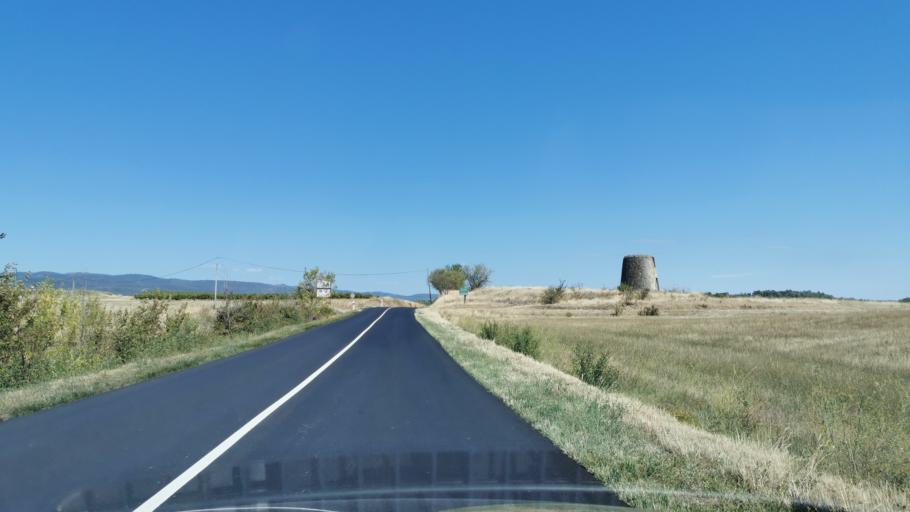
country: FR
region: Languedoc-Roussillon
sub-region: Departement de l'Aude
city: Conques-sur-Orbiel
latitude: 43.2768
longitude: 2.4277
